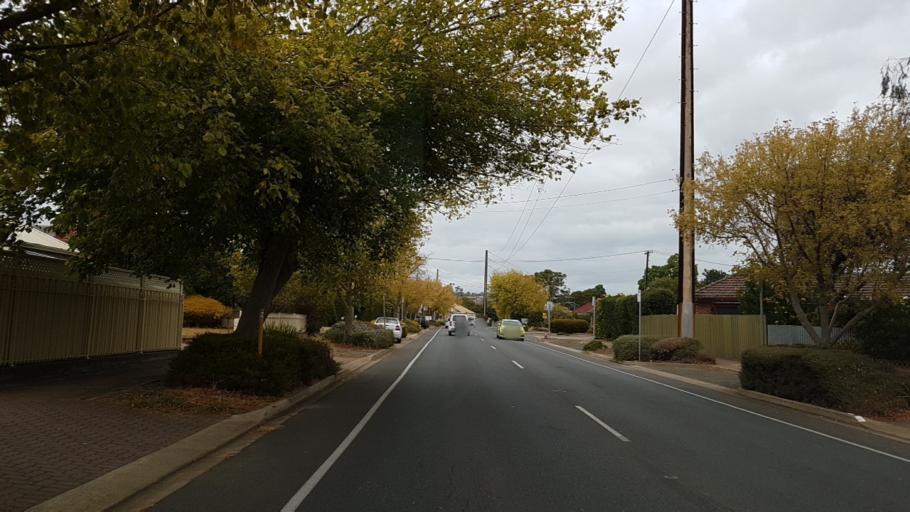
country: AU
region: South Australia
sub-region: Marion
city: Marion
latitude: -35.0113
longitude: 138.5662
